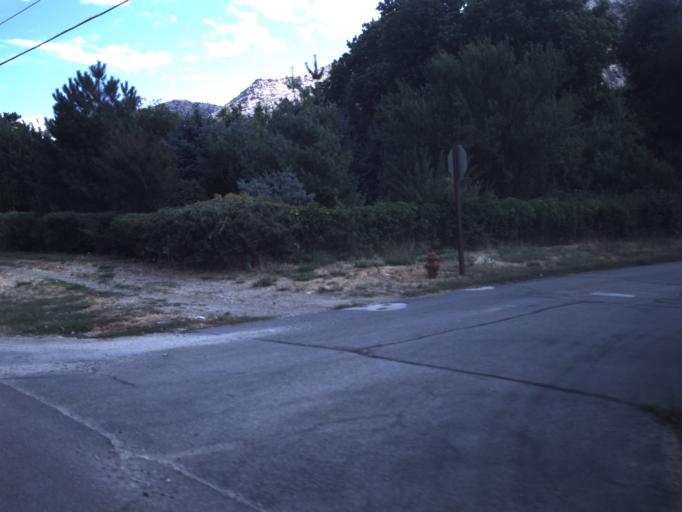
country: US
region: Utah
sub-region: Box Elder County
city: Willard
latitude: 41.4069
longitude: -112.0363
